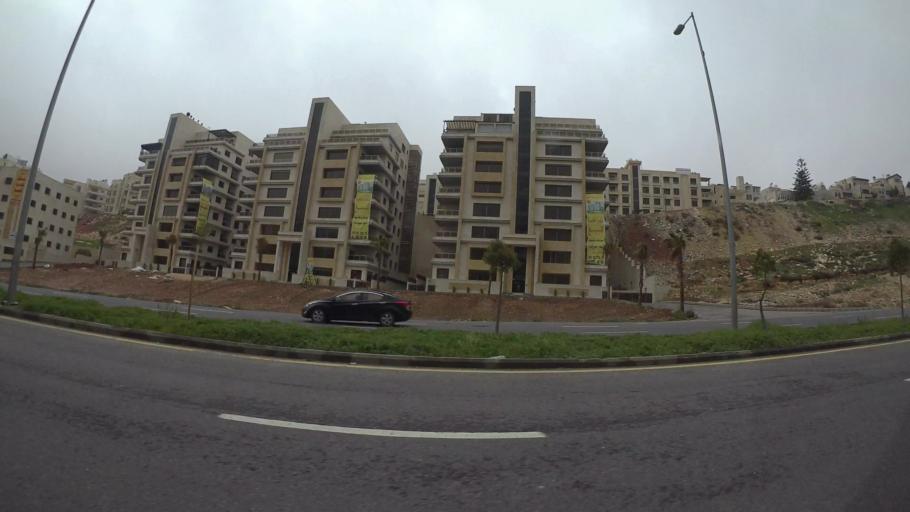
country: JO
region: Amman
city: Al Bunayyat ash Shamaliyah
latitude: 31.9385
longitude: 35.8709
